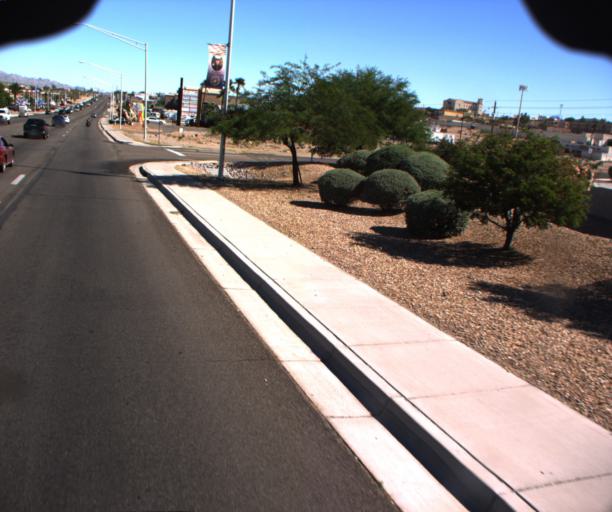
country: US
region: Arizona
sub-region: Mohave County
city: Bullhead City
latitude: 35.0892
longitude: -114.5979
